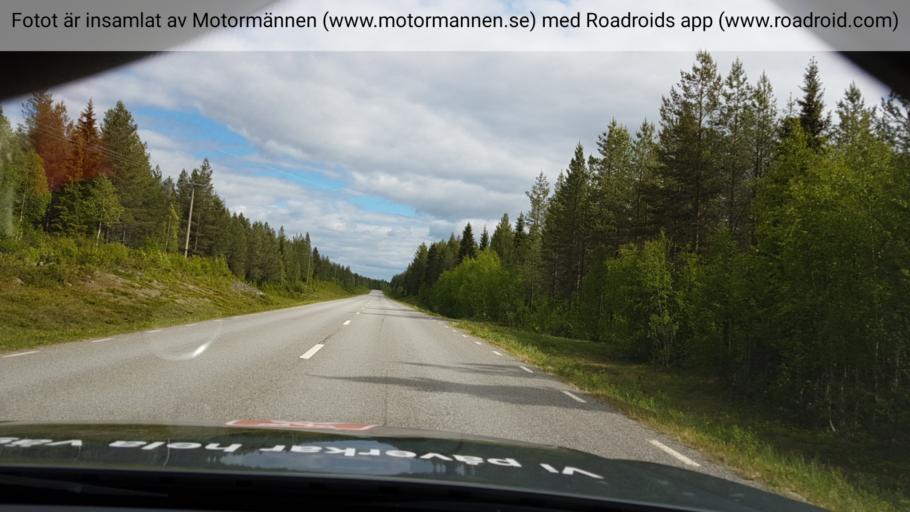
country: SE
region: Jaemtland
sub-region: Stroemsunds Kommun
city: Stroemsund
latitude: 64.2820
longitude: 15.3593
